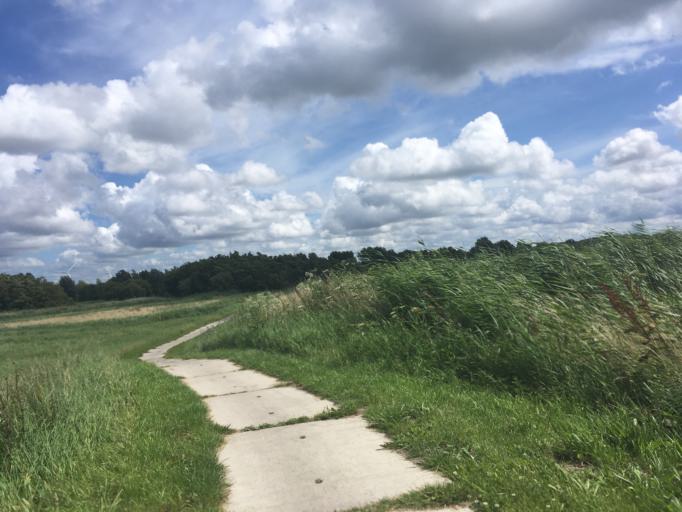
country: NL
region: North Holland
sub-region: Gemeente Haarlem
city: Haarlem
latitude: 52.4048
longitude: 4.7166
